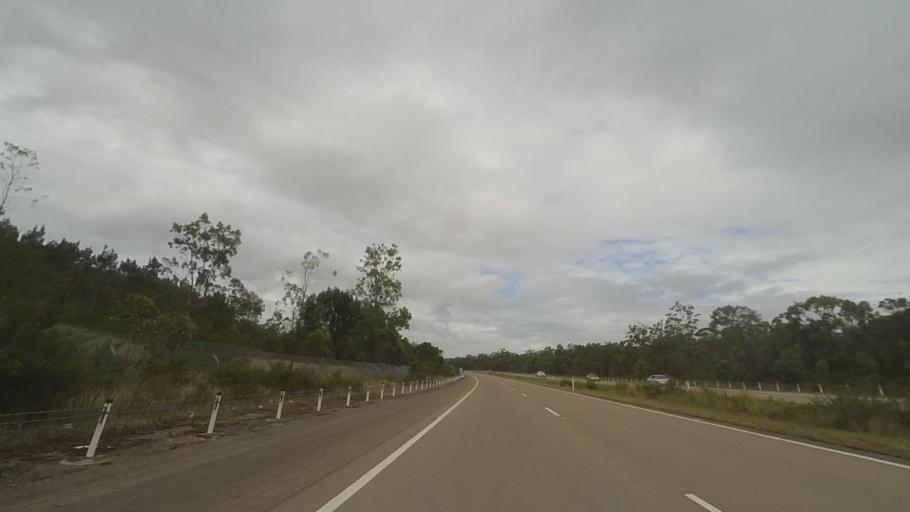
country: AU
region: New South Wales
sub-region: Port Stephens Shire
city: Medowie
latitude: -32.6463
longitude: 151.9220
